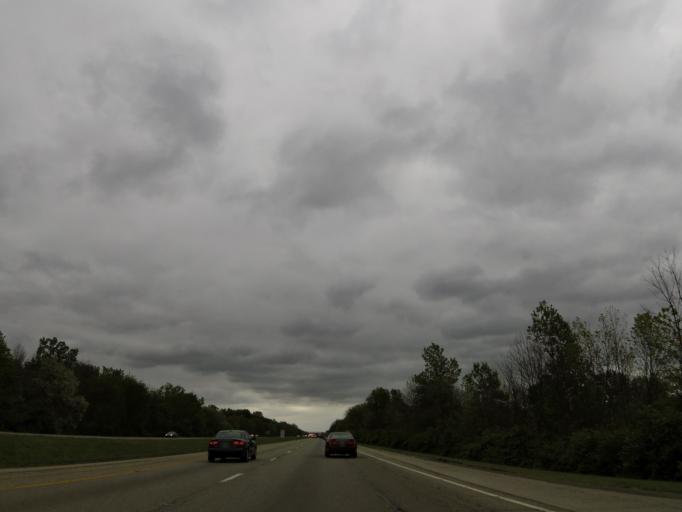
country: US
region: Ohio
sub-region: Warren County
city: Morrow
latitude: 39.4132
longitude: -84.1455
